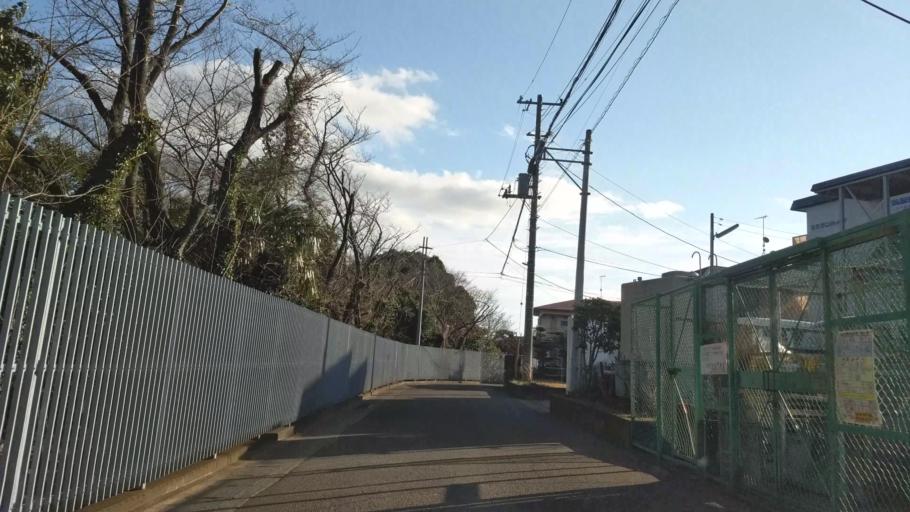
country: JP
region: Kanagawa
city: Isehara
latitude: 35.3649
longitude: 139.2707
